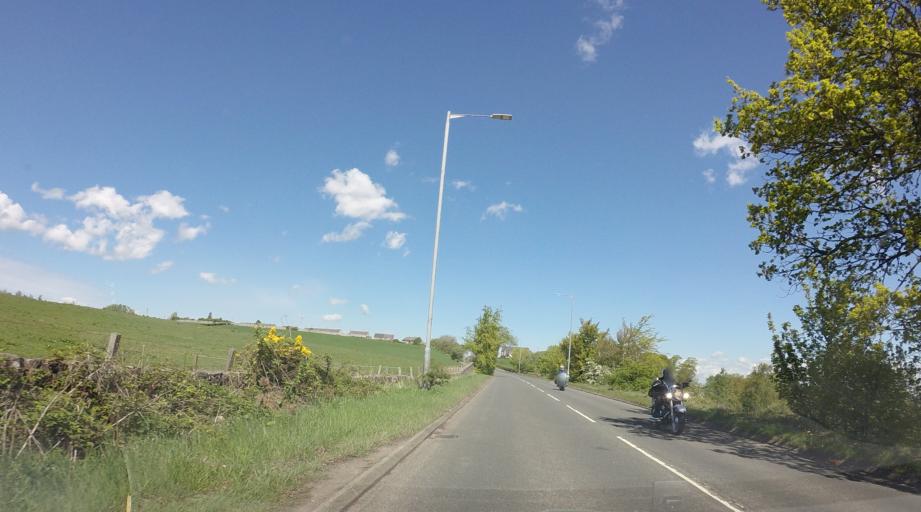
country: GB
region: Scotland
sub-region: Falkirk
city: Polmont
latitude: 55.9644
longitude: -3.6936
